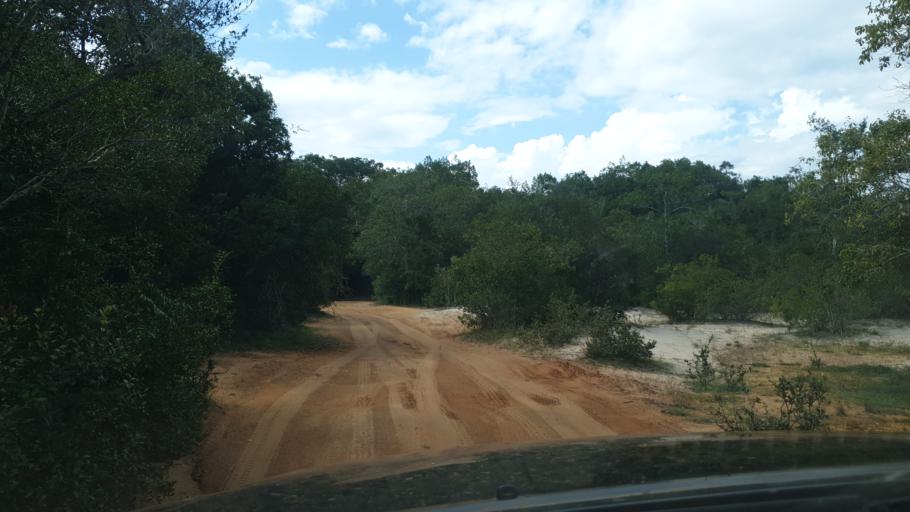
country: LK
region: North Central
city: Anuradhapura
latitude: 8.4197
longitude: 80.0149
